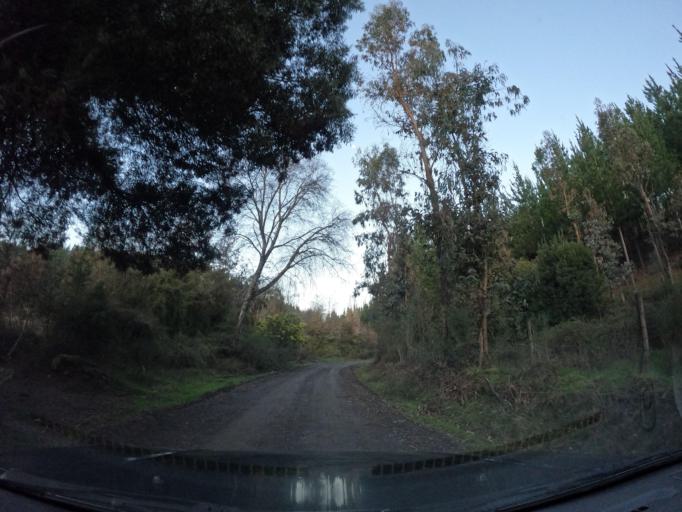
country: CL
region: Biobio
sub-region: Provincia de Concepcion
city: Chiguayante
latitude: -36.9934
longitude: -72.8344
